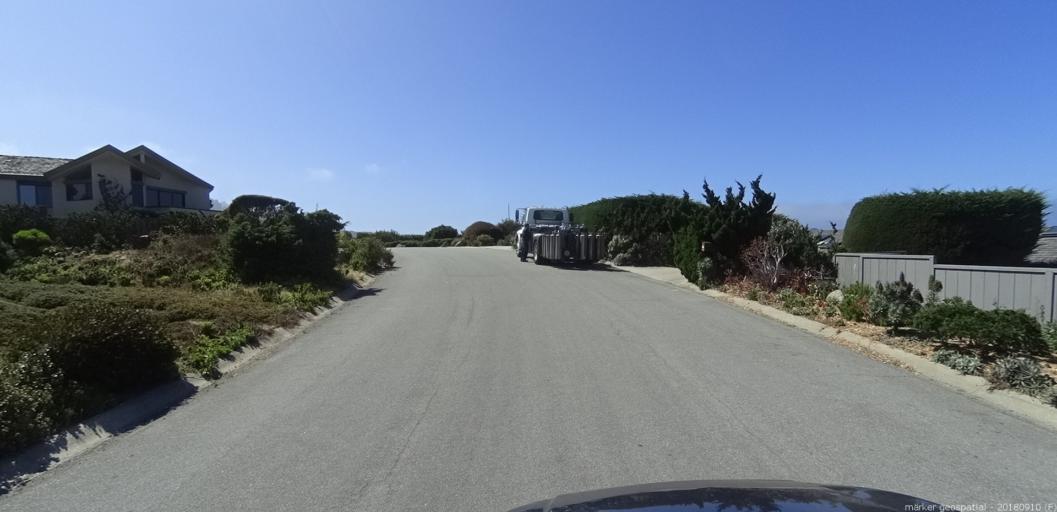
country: US
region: California
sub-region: Monterey County
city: Carmel-by-the-Sea
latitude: 36.5334
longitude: -121.9256
